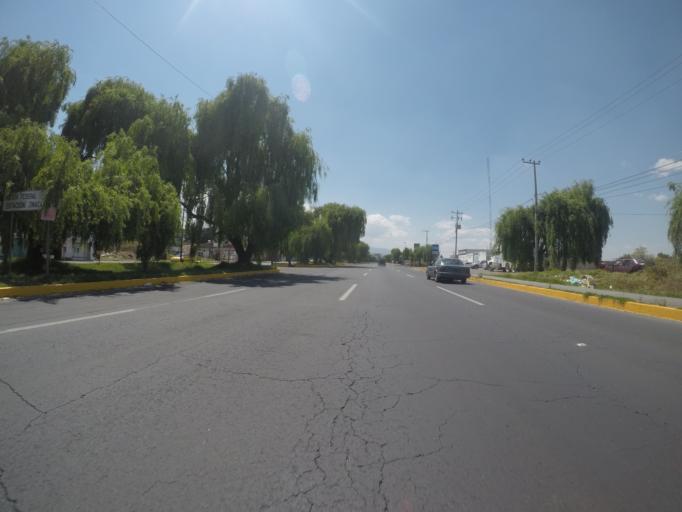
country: MX
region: Mexico
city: Cacalomacan
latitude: 19.2568
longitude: -99.7010
